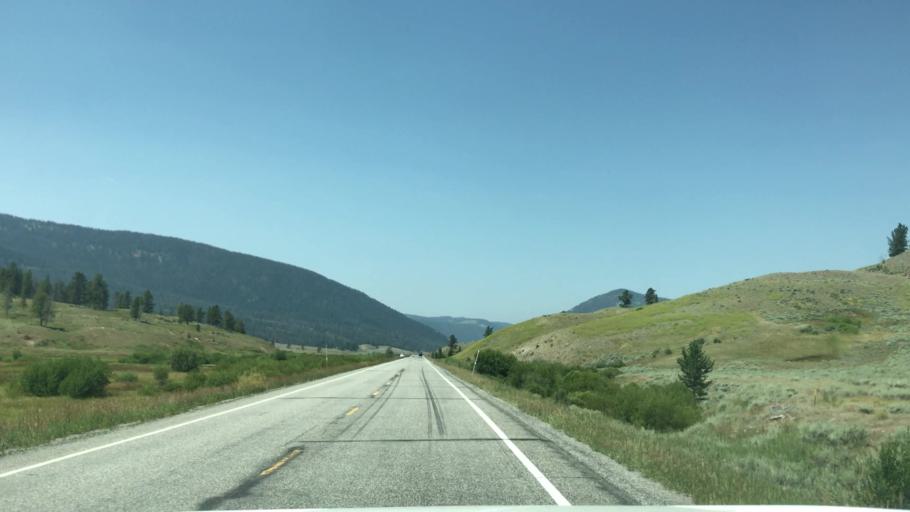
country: US
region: Montana
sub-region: Gallatin County
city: Big Sky
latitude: 45.0393
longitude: -111.1208
